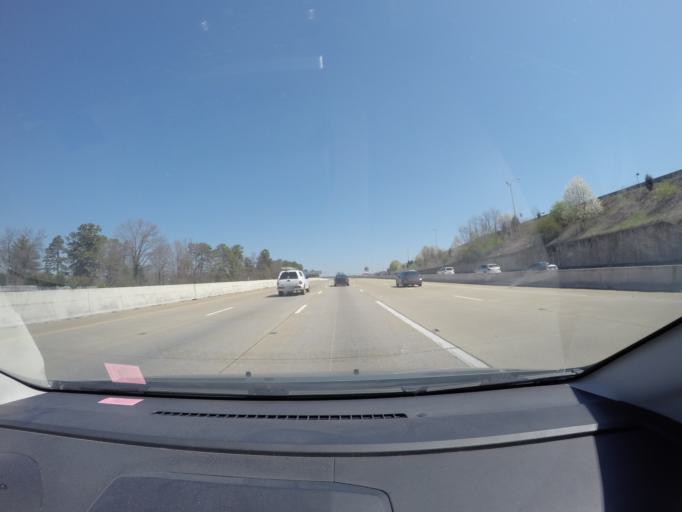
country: US
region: Tennessee
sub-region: Hamilton County
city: East Brainerd
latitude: 35.0330
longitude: -85.1661
